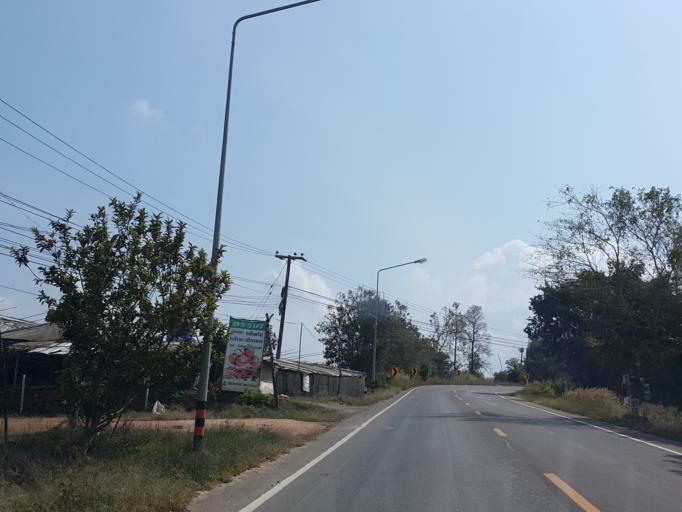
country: TH
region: Chiang Mai
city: Hot
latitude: 18.0860
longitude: 98.3646
